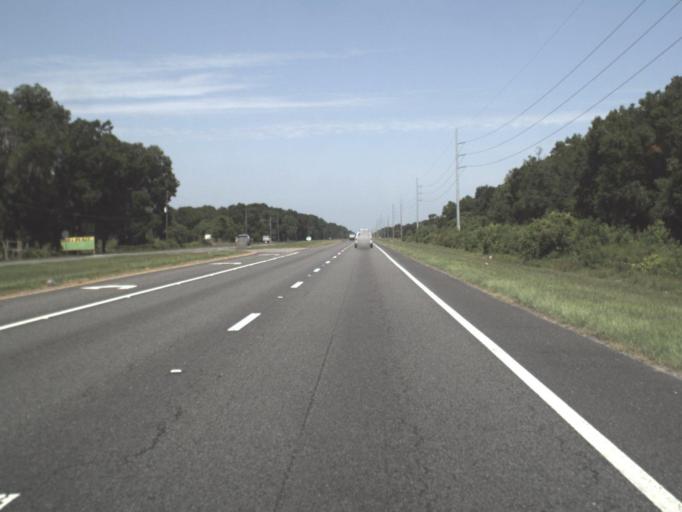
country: US
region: Florida
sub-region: Dixie County
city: Cross City
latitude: 29.6040
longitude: -83.0288
